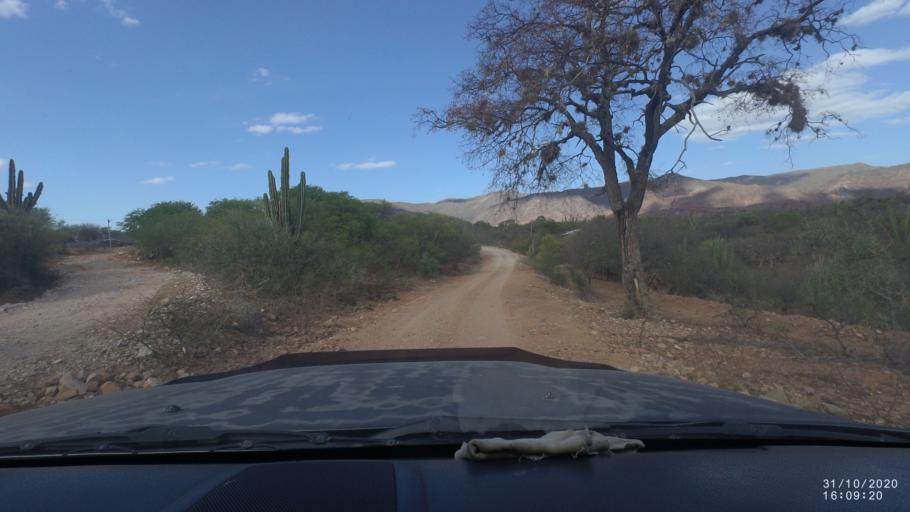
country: BO
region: Chuquisaca
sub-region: Provincia Zudanez
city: Mojocoya
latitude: -18.3867
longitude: -64.6372
